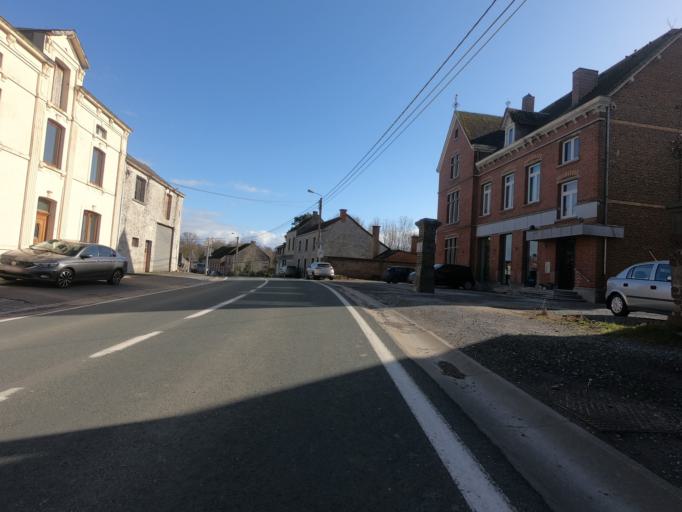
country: BE
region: Wallonia
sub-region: Province de Namur
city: Mettet
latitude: 50.2966
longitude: 4.7191
